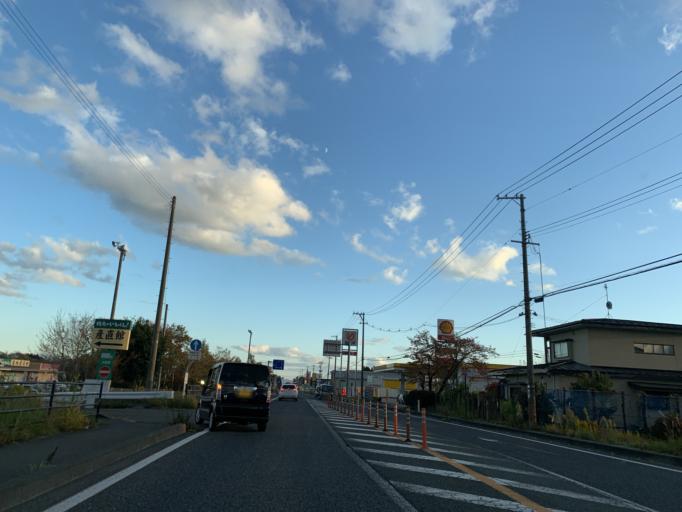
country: JP
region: Iwate
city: Kitakami
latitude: 39.2198
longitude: 141.0994
